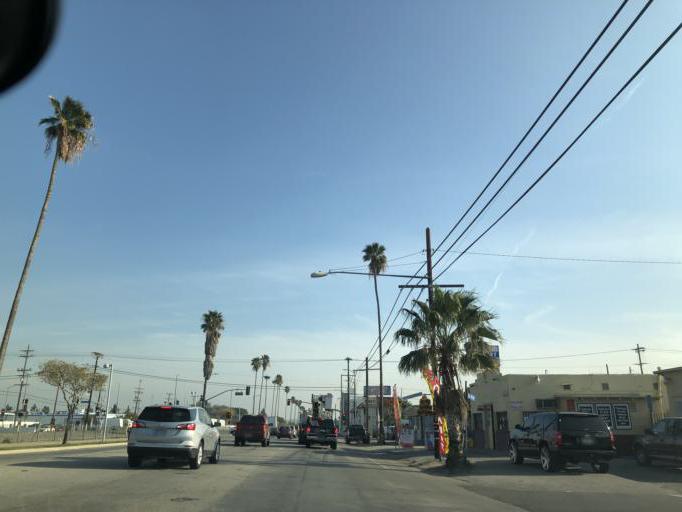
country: US
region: California
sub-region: Los Angeles County
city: San Fernando
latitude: 34.3051
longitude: -118.4671
